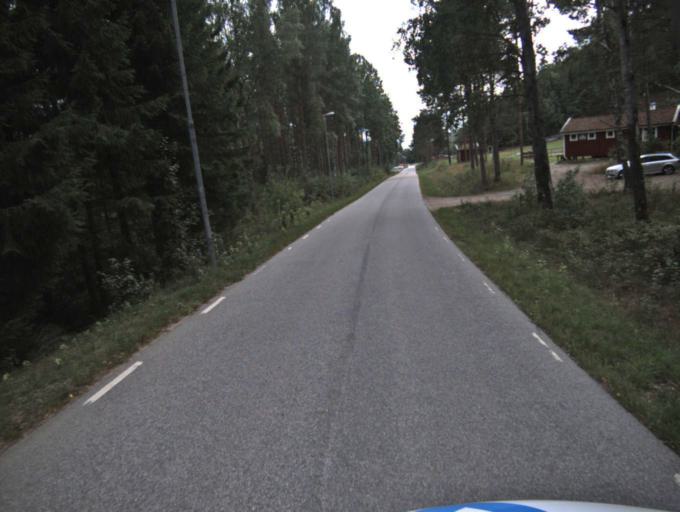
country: SE
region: Vaestra Goetaland
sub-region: Ulricehamns Kommun
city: Ulricehamn
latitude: 57.8228
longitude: 13.4153
